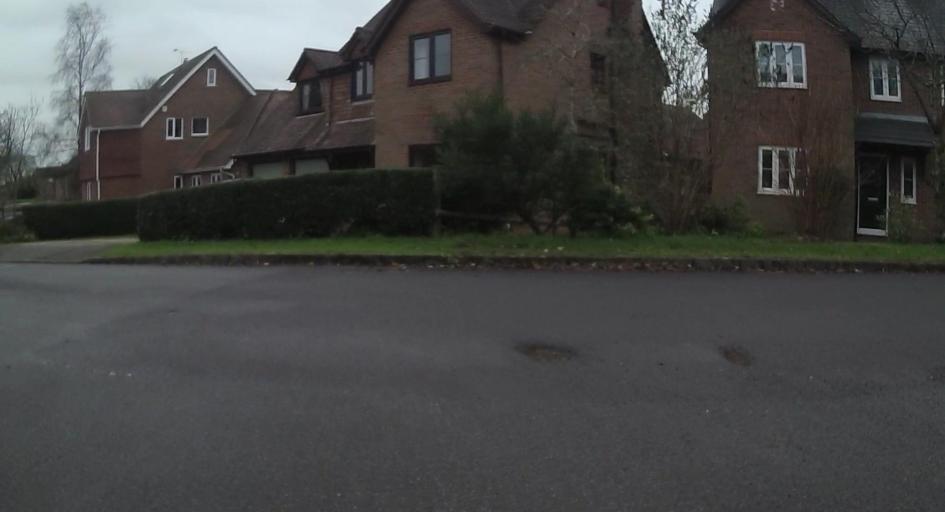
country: GB
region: England
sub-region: Hampshire
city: Four Marks
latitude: 51.1080
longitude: -1.0587
